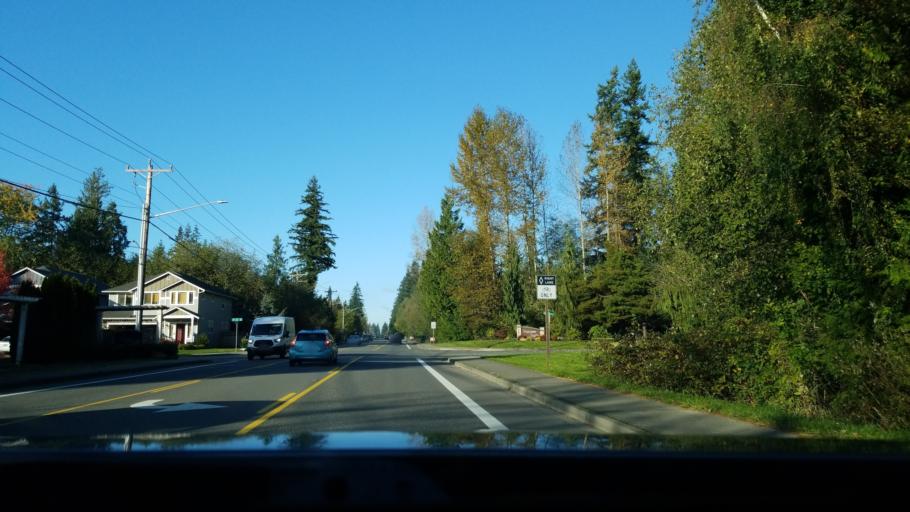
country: US
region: Washington
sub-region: Snohomish County
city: Mill Creek
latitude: 47.8836
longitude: -122.1853
